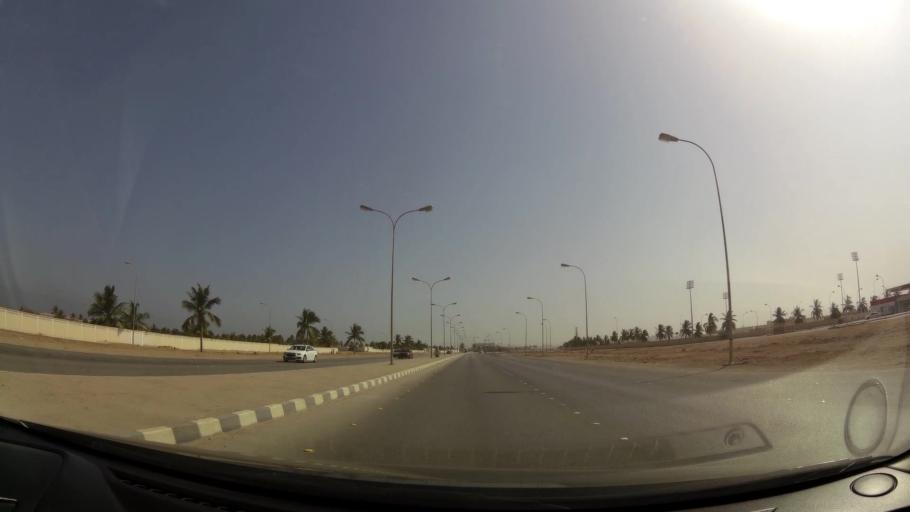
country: OM
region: Zufar
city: Salalah
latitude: 16.9934
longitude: 54.0288
